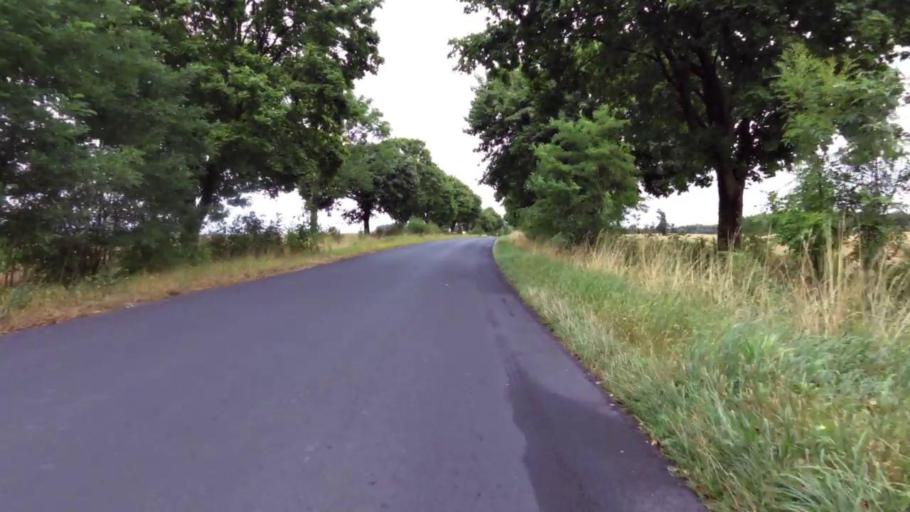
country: PL
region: West Pomeranian Voivodeship
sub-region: Powiat mysliborski
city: Debno
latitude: 52.8382
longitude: 14.6708
